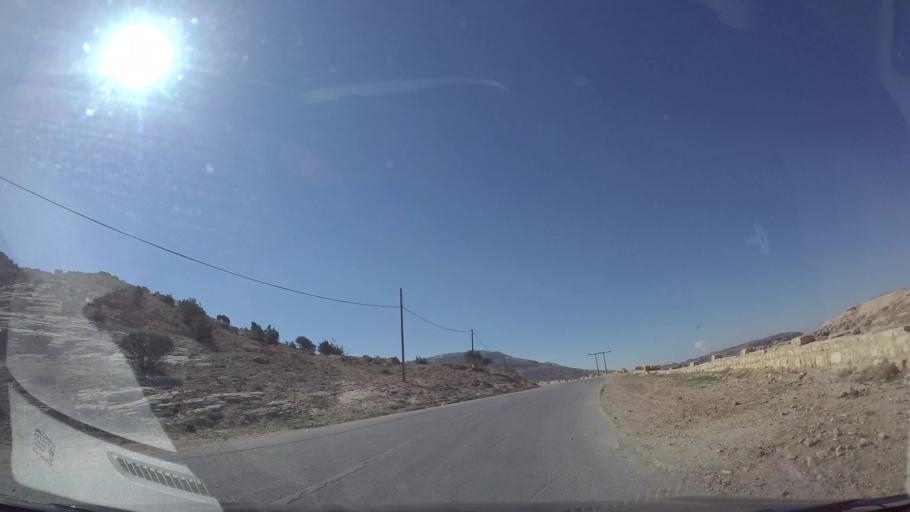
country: JO
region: Ma'an
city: Petra
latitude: 30.3341
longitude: 35.4683
